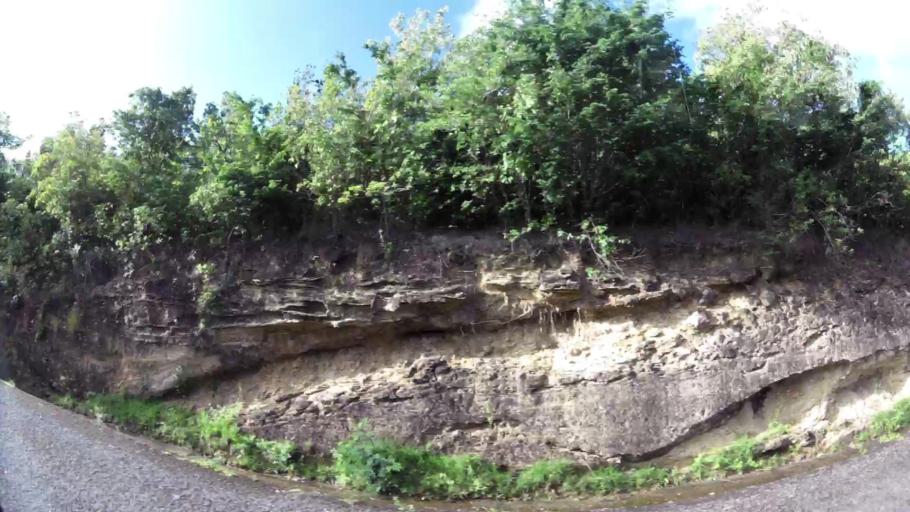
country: LC
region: Anse-la-Raye
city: Canaries
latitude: 13.8980
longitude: -61.0629
